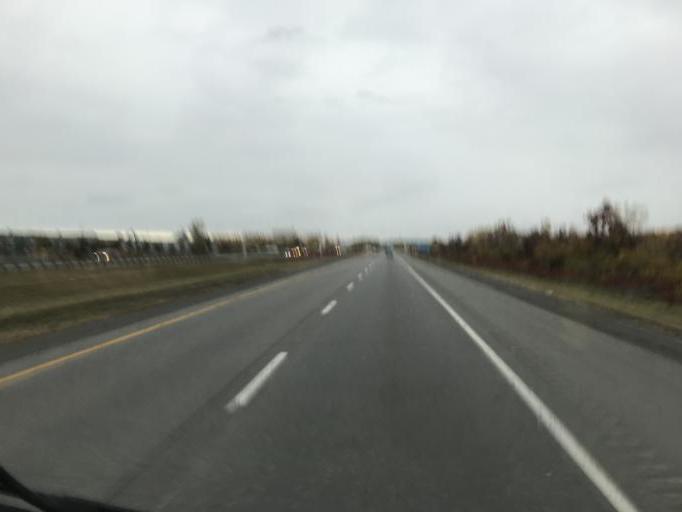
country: CA
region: Quebec
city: Bois-des-Filion
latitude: 45.6826
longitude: -73.7606
